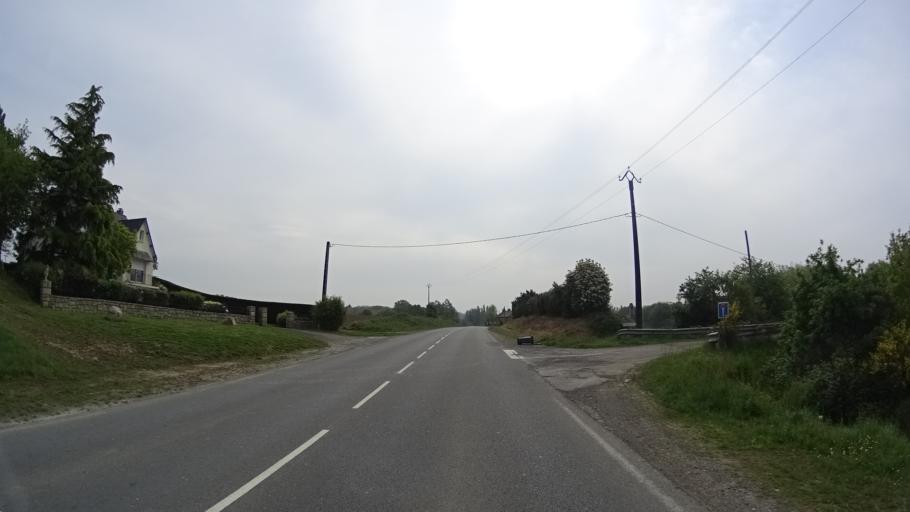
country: FR
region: Brittany
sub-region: Departement d'Ille-et-Vilaine
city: Vignoc
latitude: 48.2510
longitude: -1.7602
